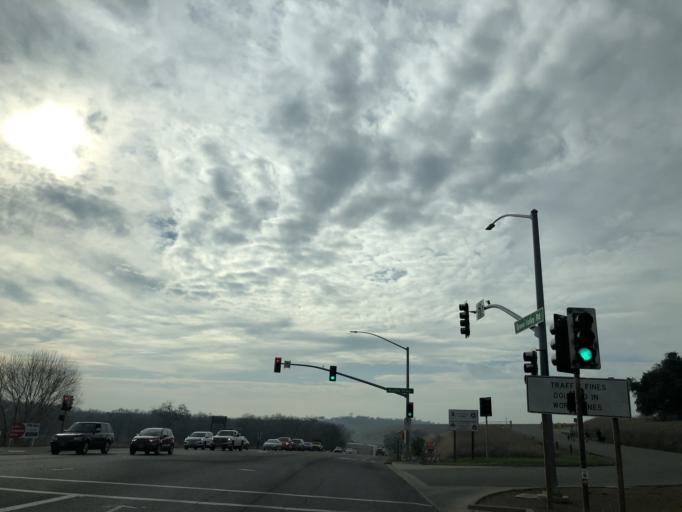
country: US
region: California
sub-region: El Dorado County
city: El Dorado Hills
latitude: 38.7015
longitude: -121.1065
